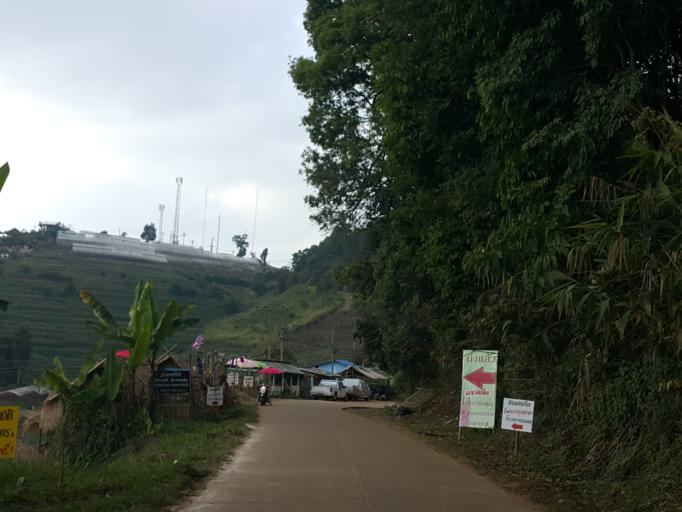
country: TH
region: Chiang Mai
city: Samoeng
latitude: 18.9347
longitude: 98.8203
